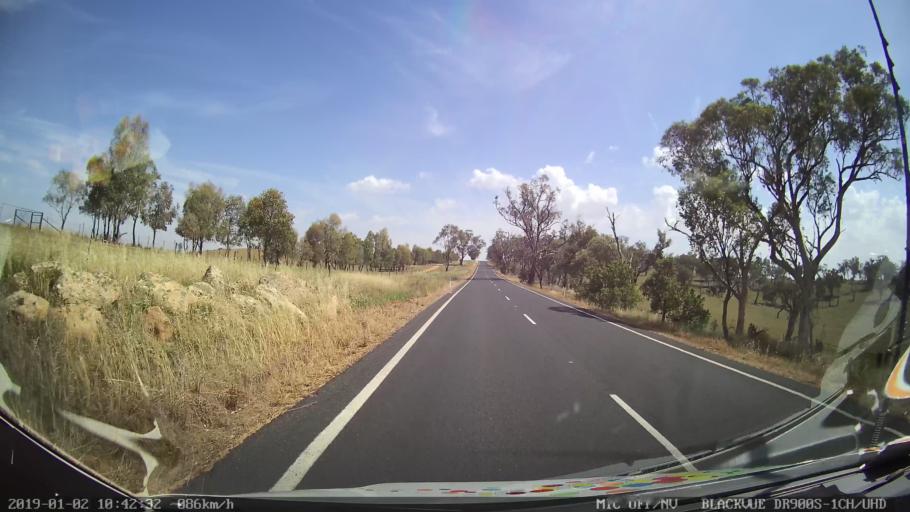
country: AU
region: New South Wales
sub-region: Cootamundra
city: Cootamundra
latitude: -34.7834
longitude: 148.3071
